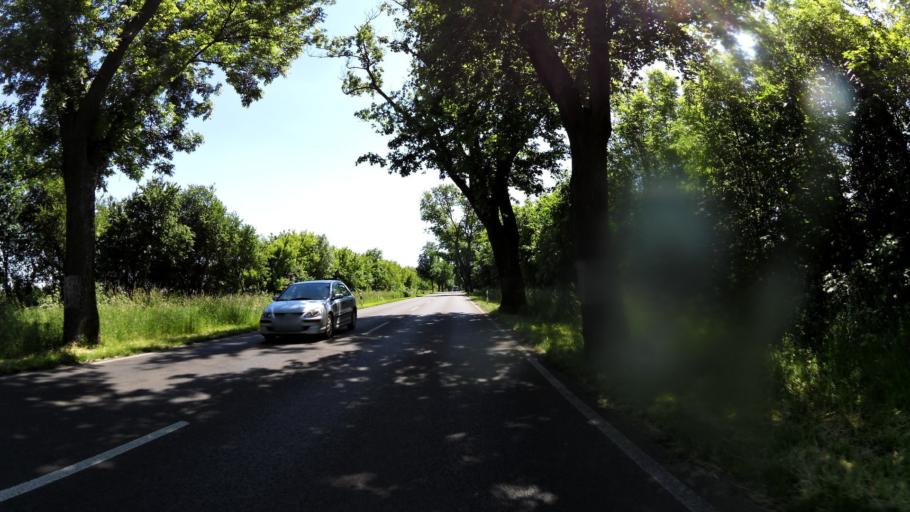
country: DE
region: Brandenburg
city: Lebus
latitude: 52.3844
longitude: 14.5186
